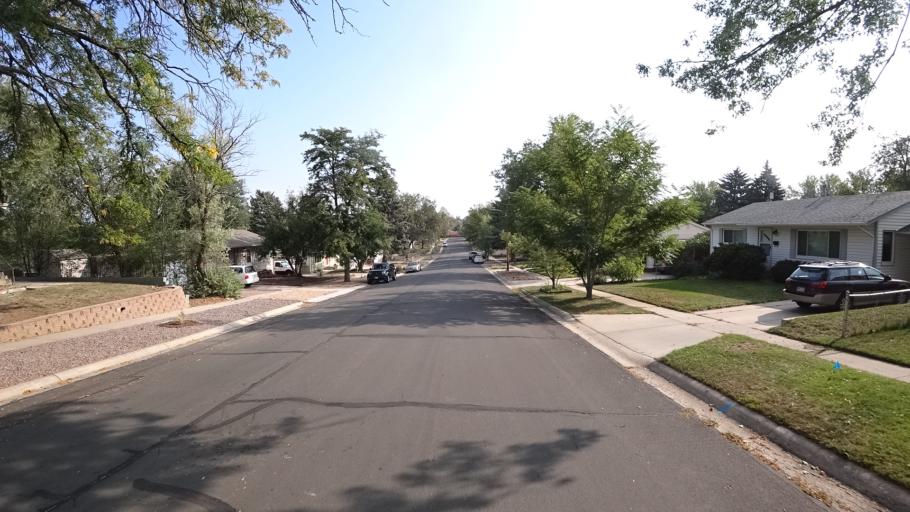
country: US
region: Colorado
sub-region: El Paso County
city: Colorado Springs
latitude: 38.8518
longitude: -104.7802
